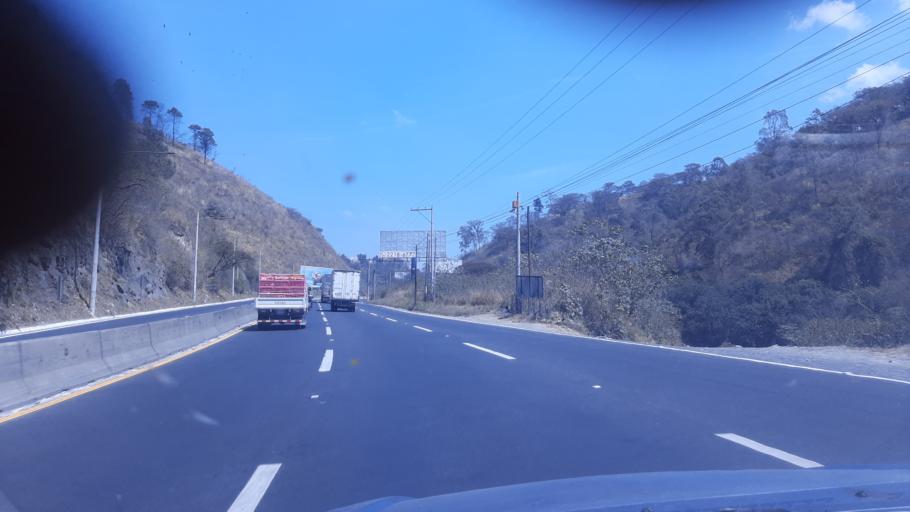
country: GT
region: Guatemala
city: Amatitlan
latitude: 14.5018
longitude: -90.6274
